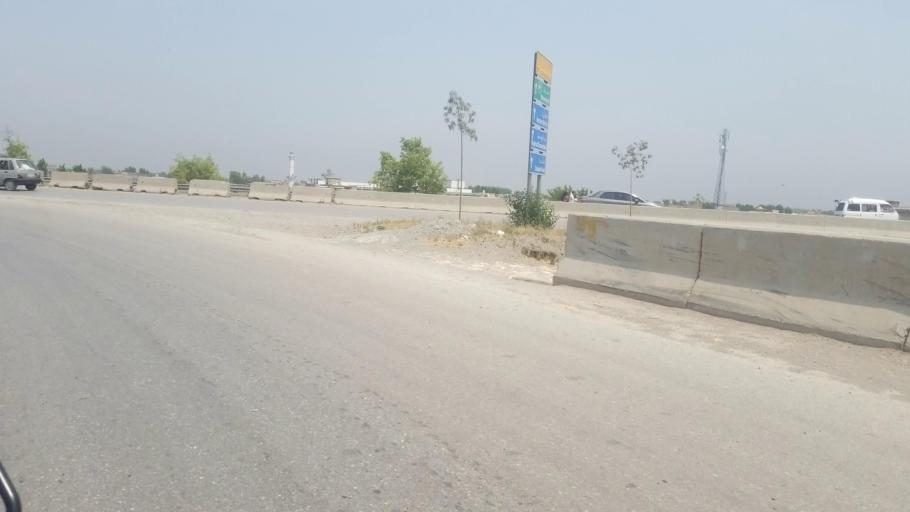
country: PK
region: Khyber Pakhtunkhwa
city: Peshawar
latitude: 34.0202
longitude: 71.6474
